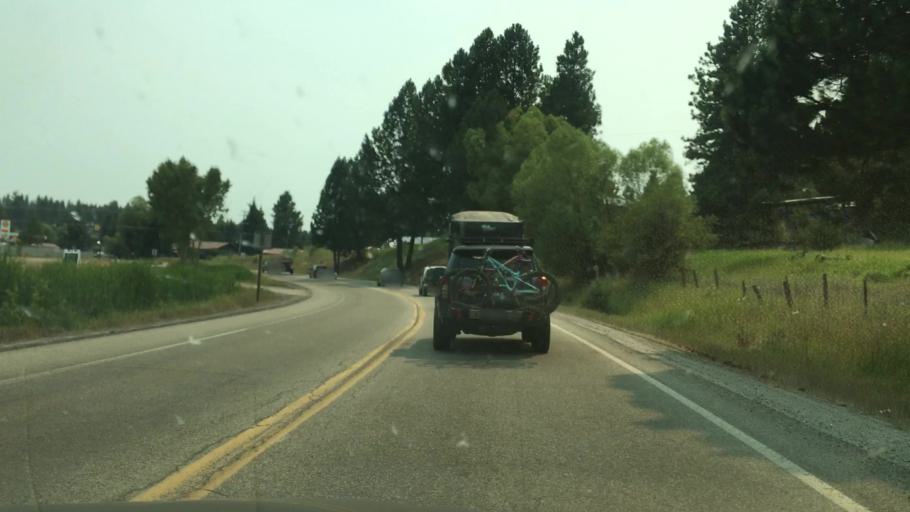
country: US
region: Idaho
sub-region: Valley County
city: Cascade
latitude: 44.5226
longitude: -116.0459
